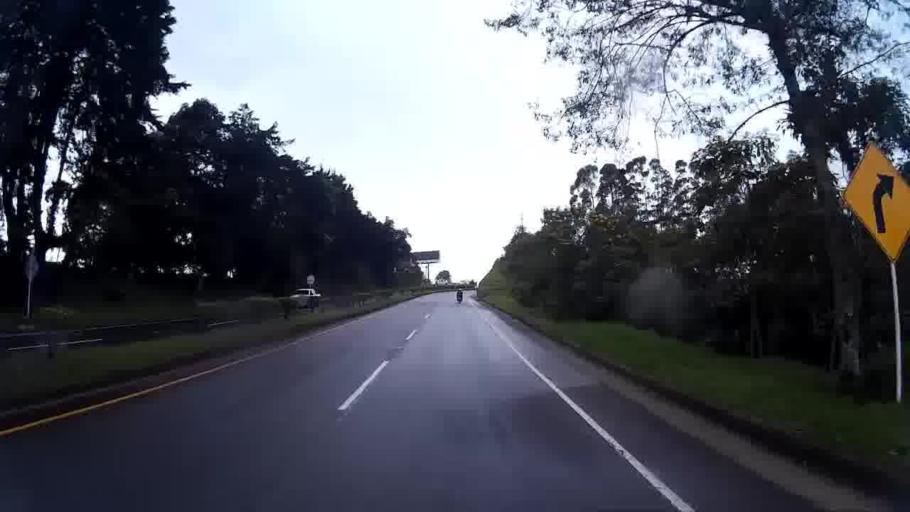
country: CO
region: Quindio
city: Salento
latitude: 4.6610
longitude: -75.5958
